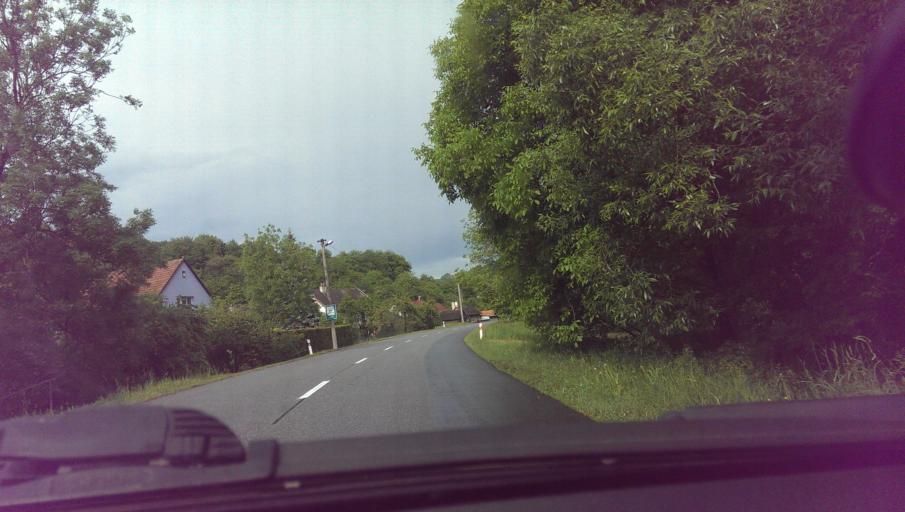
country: CZ
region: Zlin
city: Breznice
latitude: 49.1578
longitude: 17.6290
